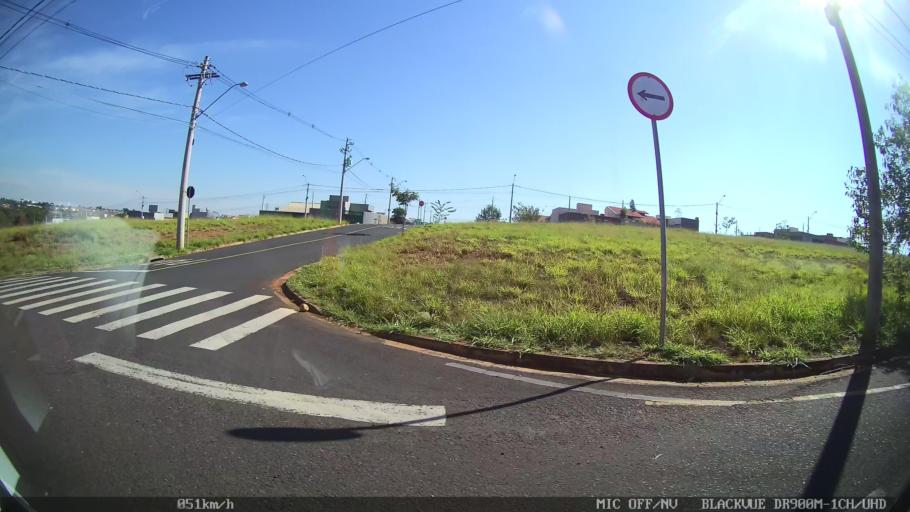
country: BR
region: Sao Paulo
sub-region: Sao Jose Do Rio Preto
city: Sao Jose do Rio Preto
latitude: -20.7684
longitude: -49.3577
